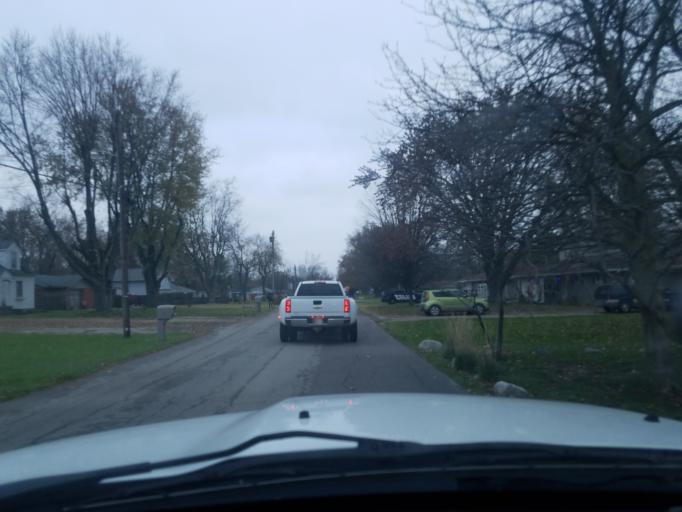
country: US
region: Indiana
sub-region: Delaware County
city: Muncie
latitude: 40.2270
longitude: -85.4058
